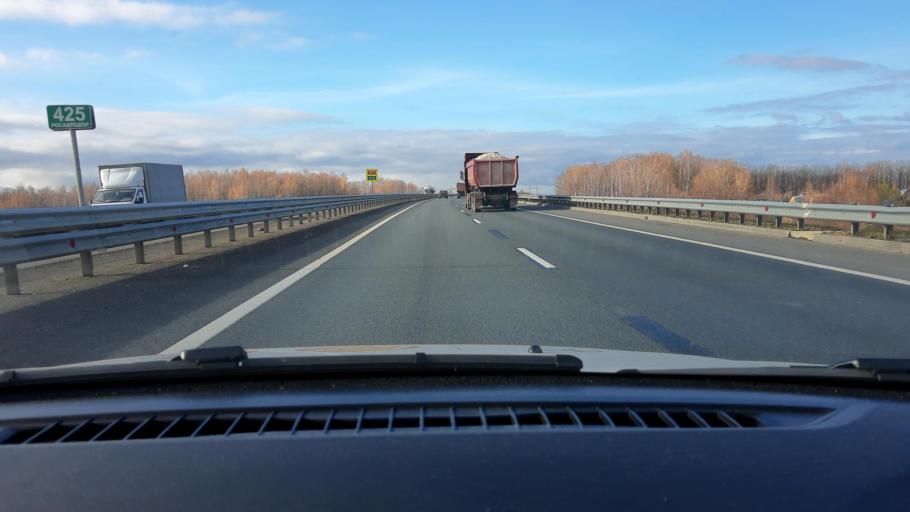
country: RU
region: Nizjnij Novgorod
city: Burevestnik
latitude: 56.1139
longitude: 43.8451
